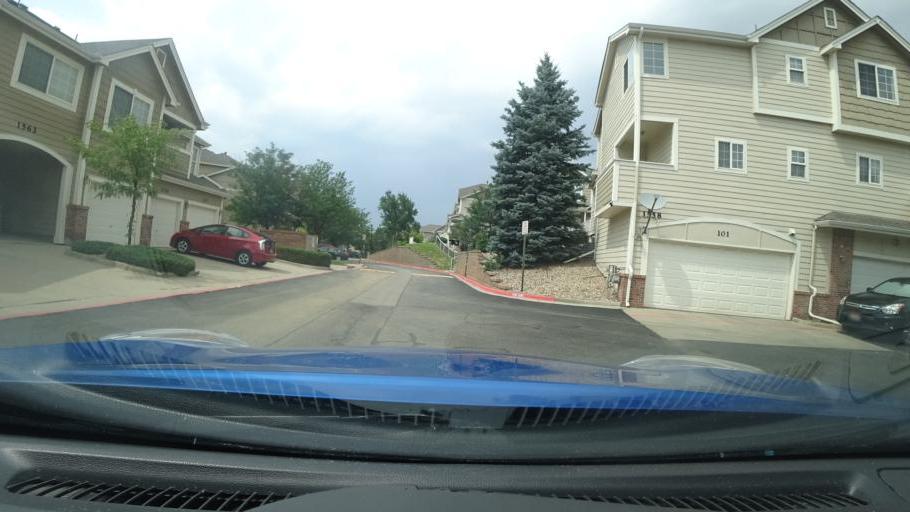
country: US
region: Colorado
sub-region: Adams County
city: Aurora
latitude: 39.6882
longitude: -104.7637
